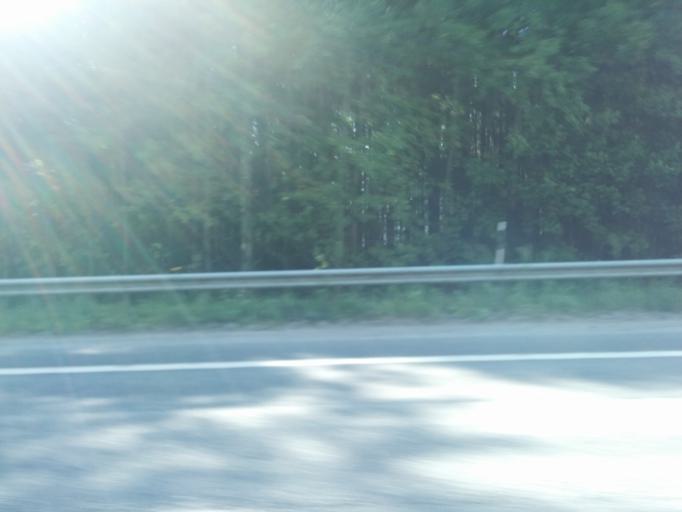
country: FI
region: Pirkanmaa
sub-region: Tampere
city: Tampere
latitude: 61.5231
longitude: 23.9278
